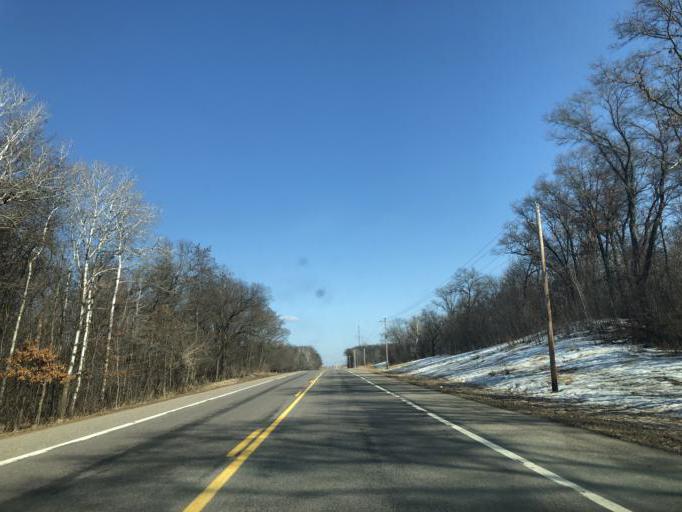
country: US
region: Minnesota
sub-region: Sherburne County
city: Becker
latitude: 45.4297
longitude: -93.8513
